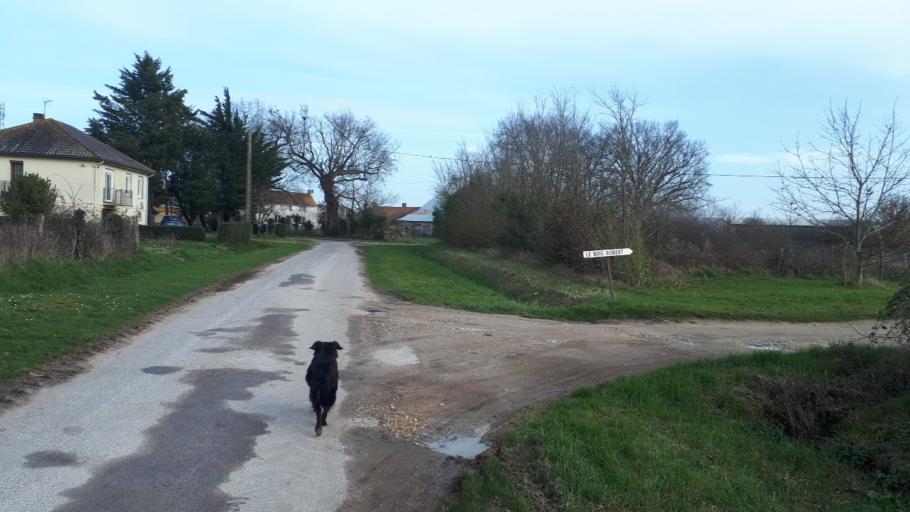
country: FR
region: Poitou-Charentes
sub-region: Departement de la Vienne
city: Archigny
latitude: 46.6200
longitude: 0.7512
